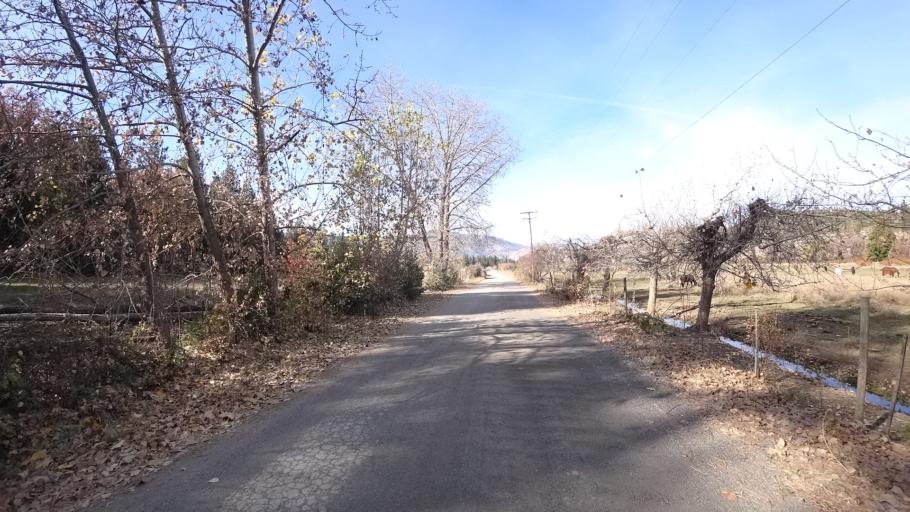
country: US
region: California
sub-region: Siskiyou County
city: Weed
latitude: 41.4315
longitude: -122.4024
